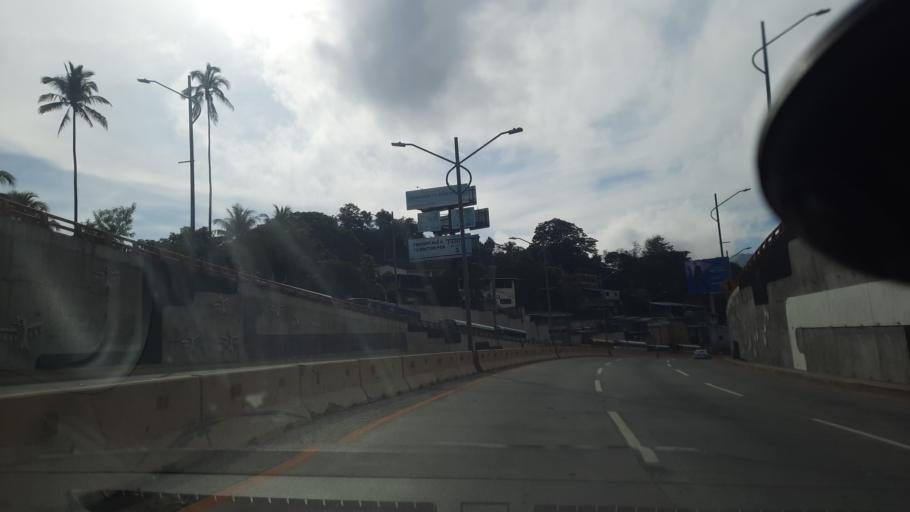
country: SV
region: San Salvador
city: San Salvador
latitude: 13.6793
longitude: -89.2099
